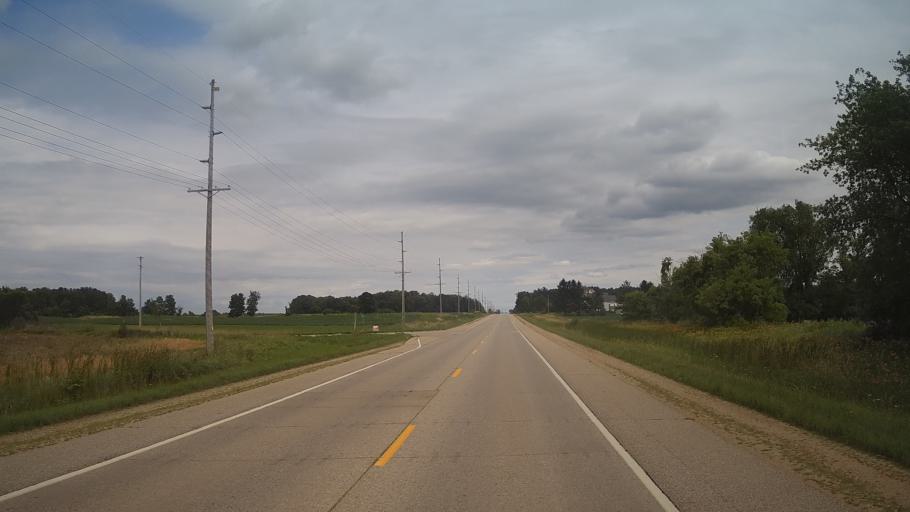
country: US
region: Wisconsin
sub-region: Waushara County
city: Redgranite
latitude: 44.0410
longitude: -89.0077
